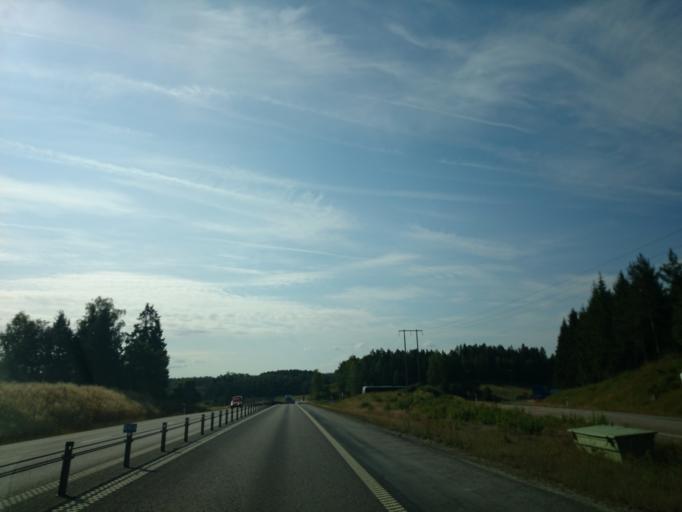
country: SE
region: OEstergoetland
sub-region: Valdemarsviks Kommun
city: Gusum
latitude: 58.2843
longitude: 16.5045
